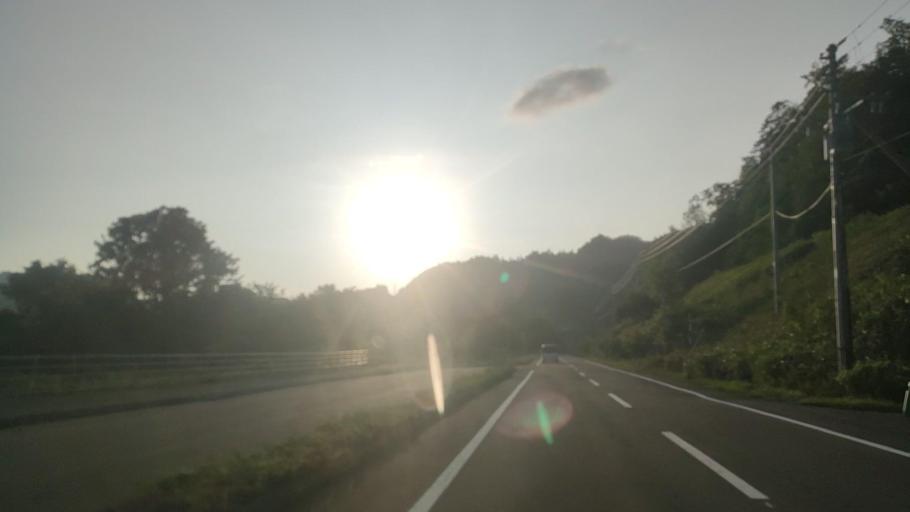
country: JP
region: Hokkaido
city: Bibai
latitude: 43.2425
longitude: 142.0253
